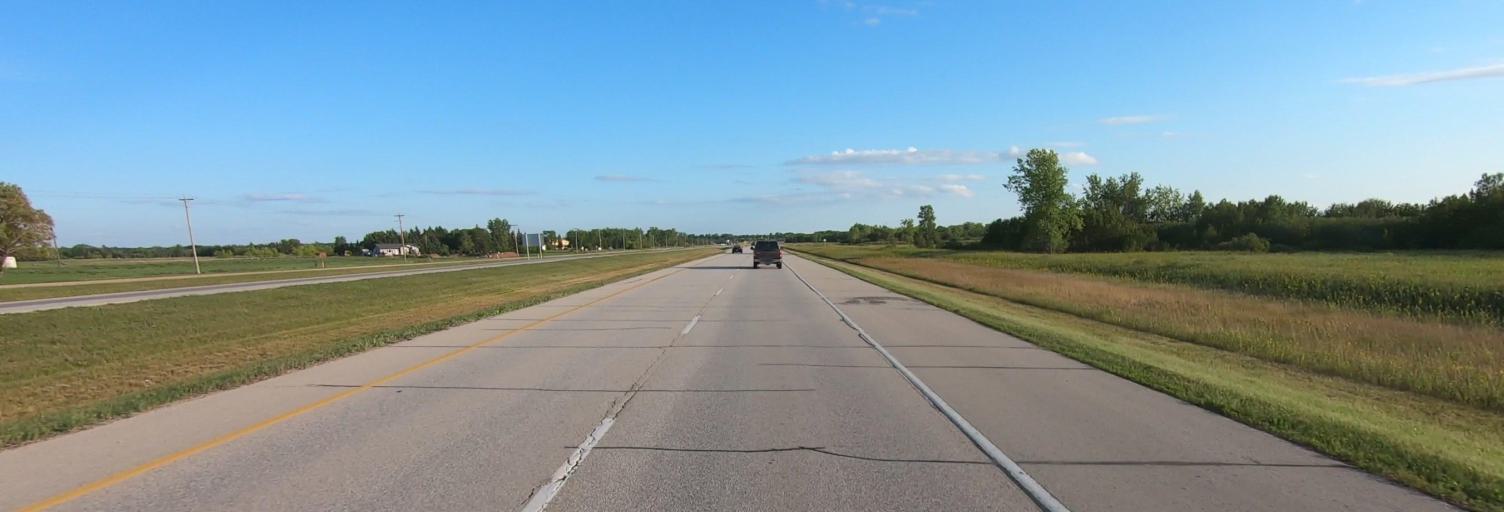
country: CA
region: Manitoba
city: Selkirk
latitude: 49.9858
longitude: -96.9761
